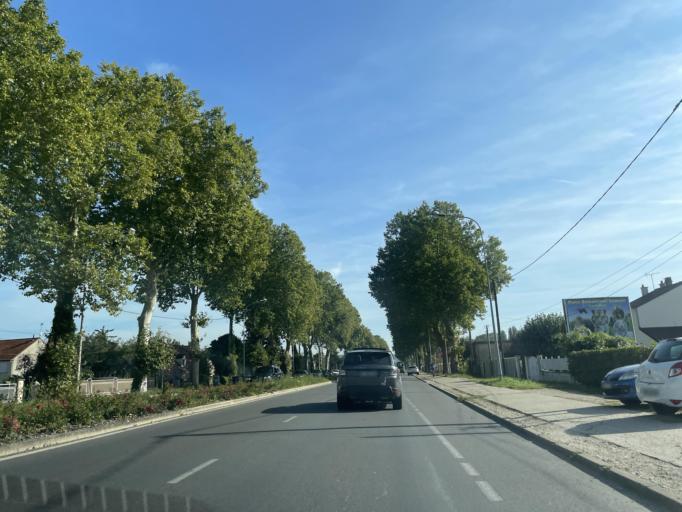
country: FR
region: Ile-de-France
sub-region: Departement de Seine-et-Marne
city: Trilport
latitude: 48.9573
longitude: 2.9329
